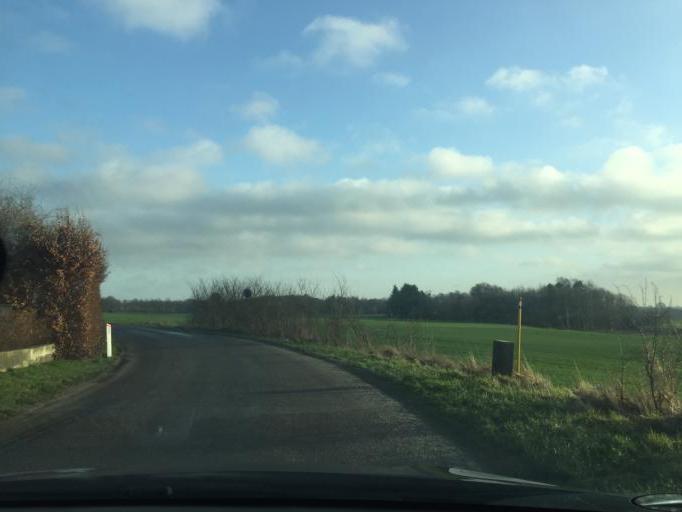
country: DK
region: South Denmark
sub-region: Faaborg-Midtfyn Kommune
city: Faaborg
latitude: 55.1997
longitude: 10.3282
